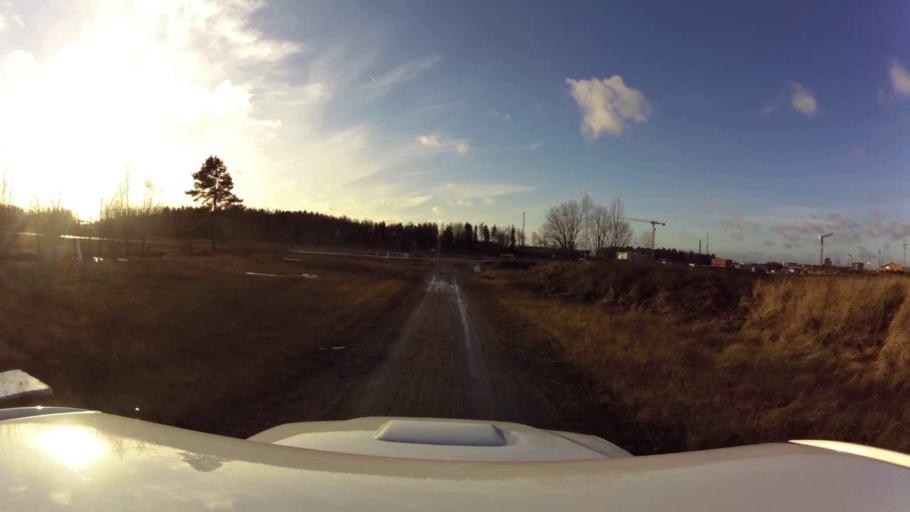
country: SE
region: OEstergoetland
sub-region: Linkopings Kommun
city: Linkoping
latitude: 58.3936
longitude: 15.5893
